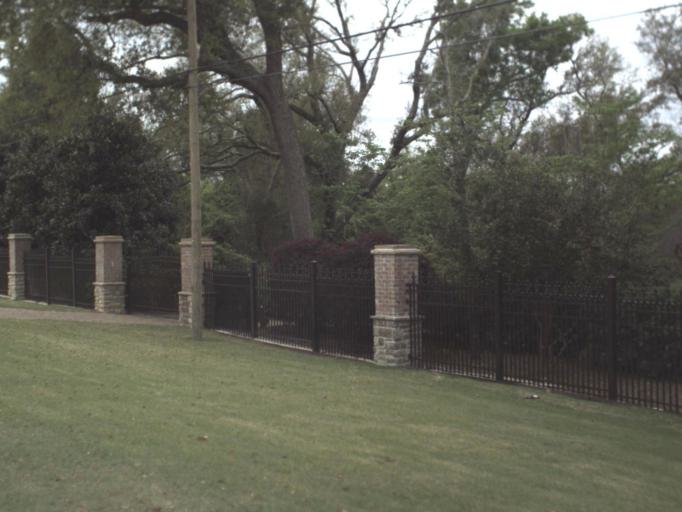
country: US
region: Florida
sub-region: Escambia County
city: East Pensacola Heights
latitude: 30.4507
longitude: -87.1920
